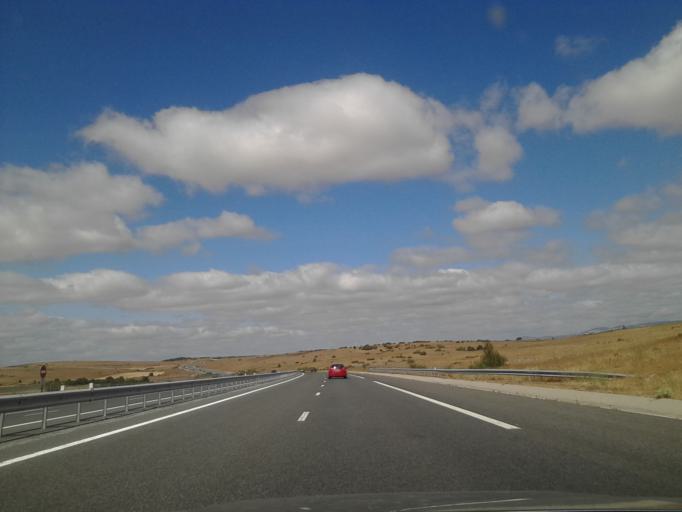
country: FR
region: Midi-Pyrenees
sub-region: Departement de l'Aveyron
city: La Cavalerie
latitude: 44.0285
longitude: 3.1013
